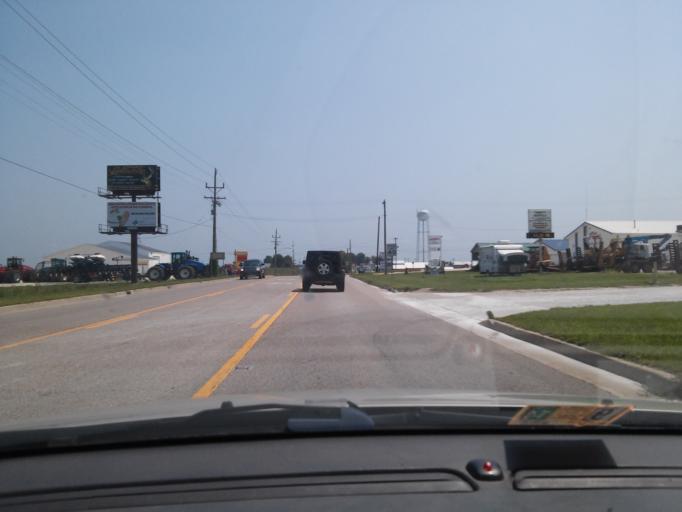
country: US
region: Illinois
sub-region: Pike County
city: Pittsfield
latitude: 39.6047
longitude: -90.8459
